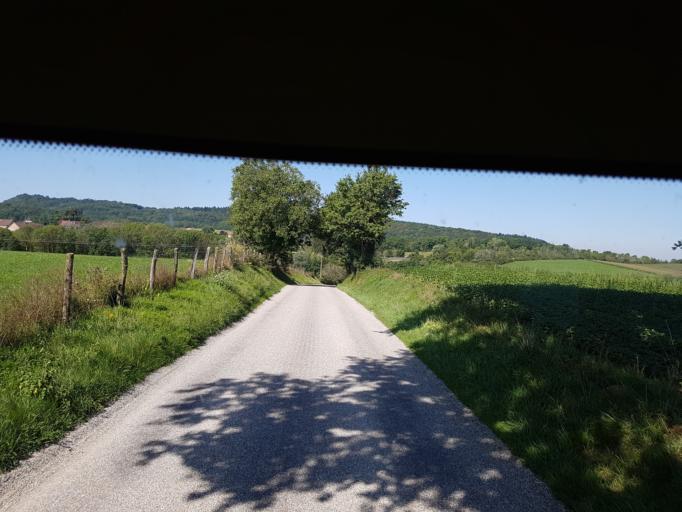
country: FR
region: Franche-Comte
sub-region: Departement du Jura
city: Lons-le-Saunier
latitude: 46.7340
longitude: 5.5637
